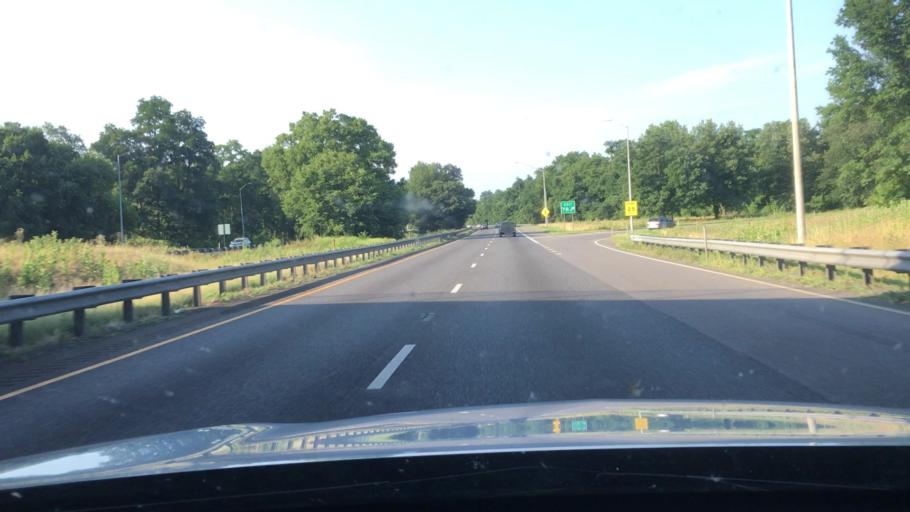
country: US
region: Maryland
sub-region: Washington County
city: Hagerstown
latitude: 39.6634
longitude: -77.7399
